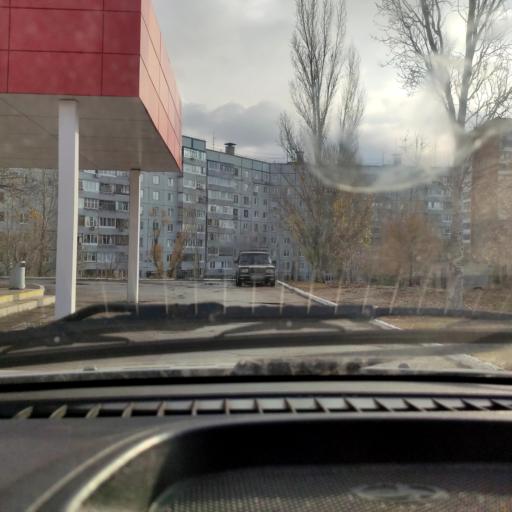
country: RU
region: Samara
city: Zhigulevsk
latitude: 53.4802
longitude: 49.4550
